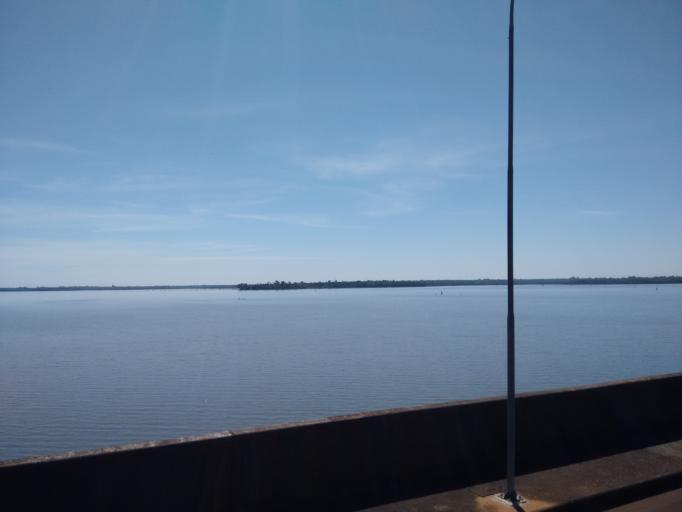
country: PY
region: Alto Parana
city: Ciudad del Este
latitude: -25.4279
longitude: -54.5645
